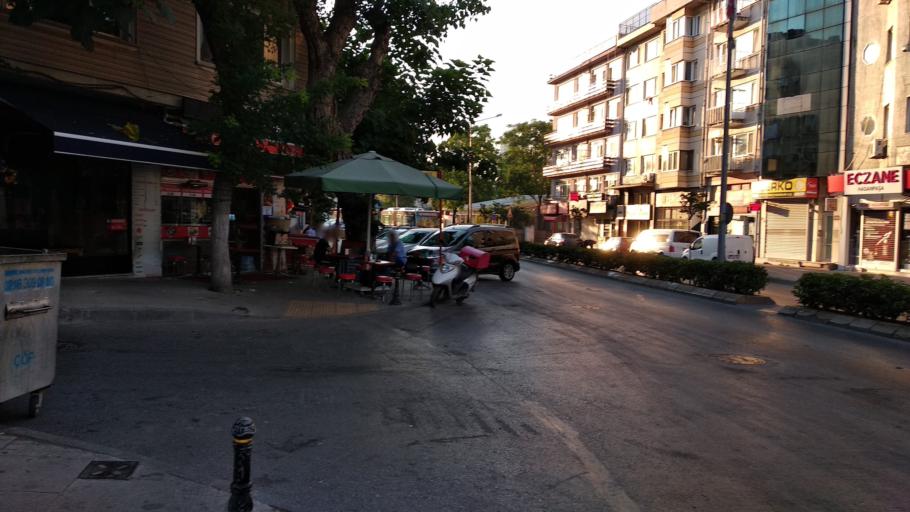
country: TR
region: Istanbul
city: UEskuedar
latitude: 40.9950
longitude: 29.0407
